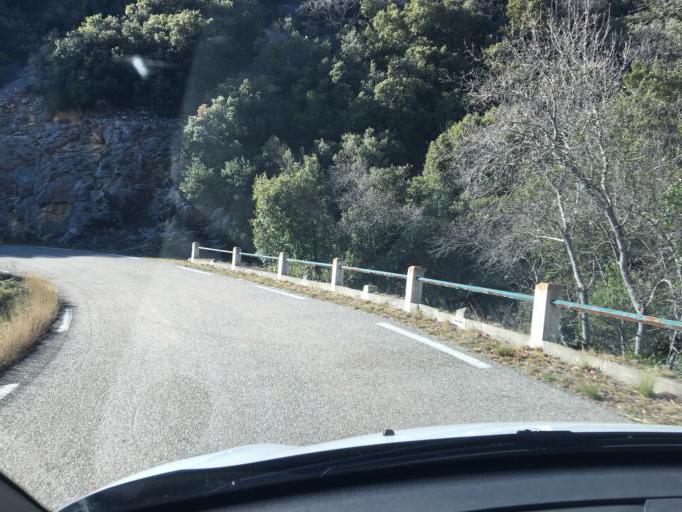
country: FR
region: Provence-Alpes-Cote d'Azur
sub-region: Departement du Vaucluse
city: Villes-sur-Auzon
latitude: 44.0675
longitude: 5.3111
